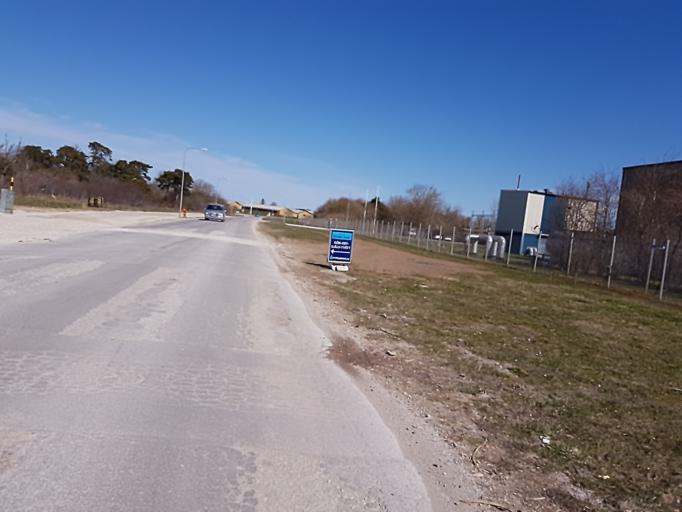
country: SE
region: Gotland
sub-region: Gotland
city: Visby
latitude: 57.6239
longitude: 18.3170
